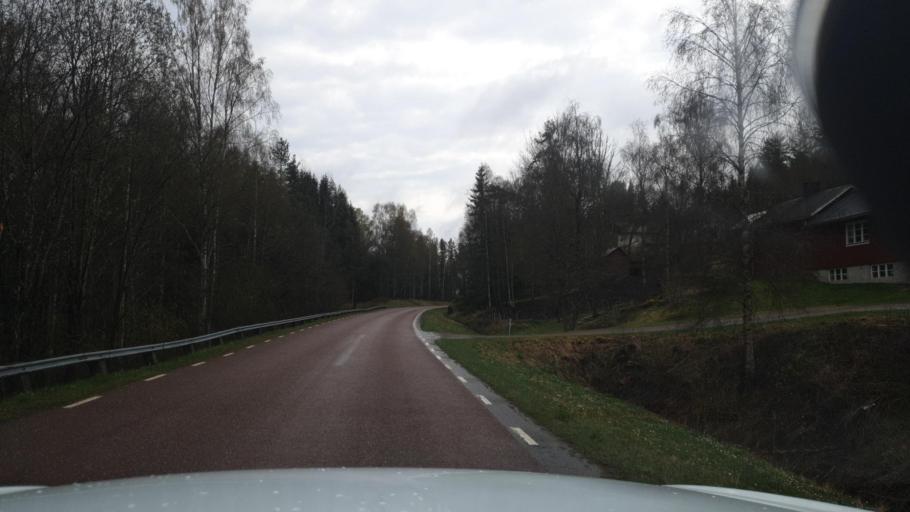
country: NO
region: Hedmark
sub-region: Eidskog
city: Skotterud
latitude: 59.7600
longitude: 12.0521
